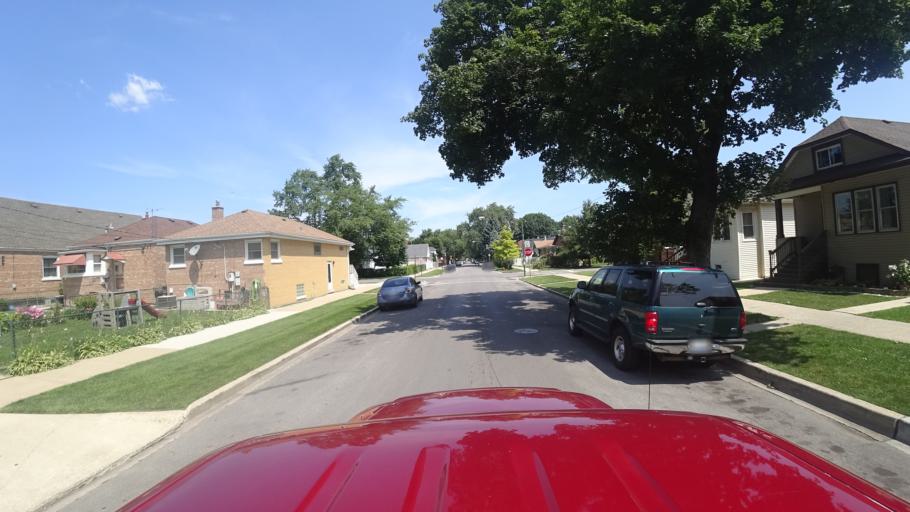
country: US
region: Illinois
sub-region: Cook County
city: Hometown
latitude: 41.7950
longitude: -87.6988
